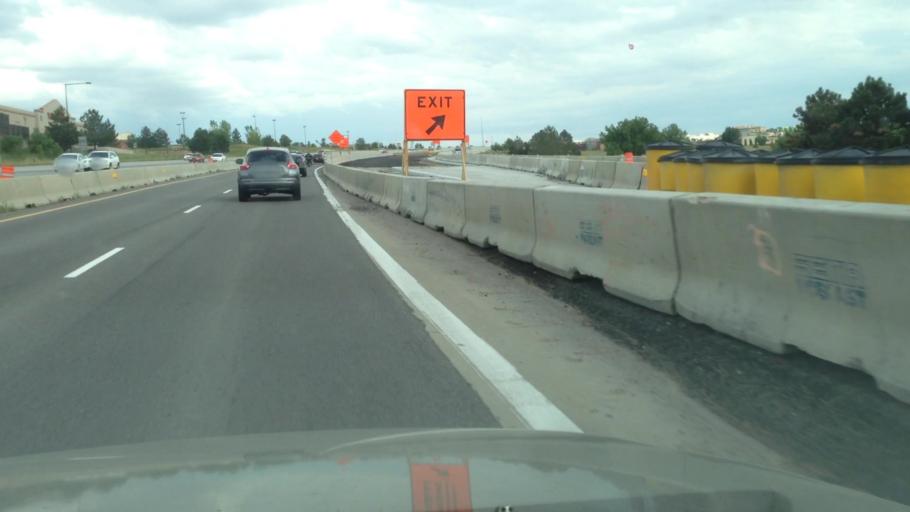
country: US
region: Colorado
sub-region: Adams County
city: Lone Tree
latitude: 39.5628
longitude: -104.8868
